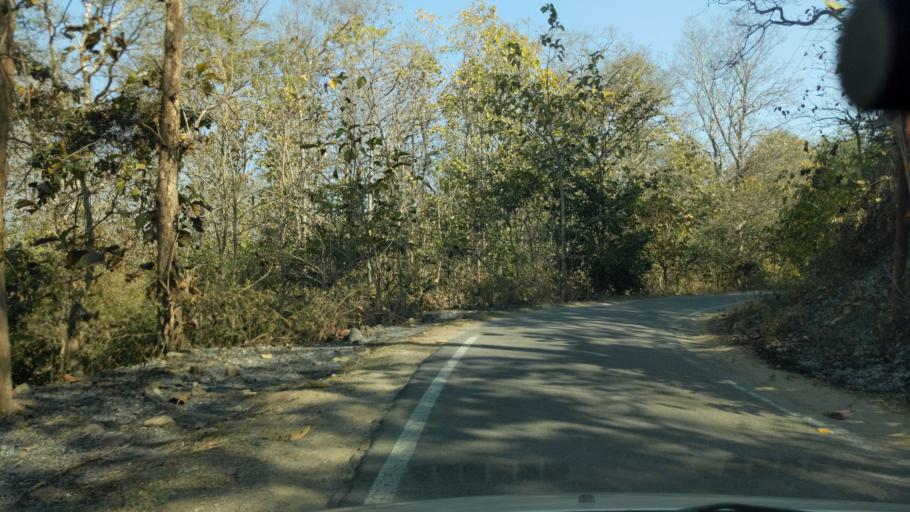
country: IN
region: Uttarakhand
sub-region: Naini Tal
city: Ramnagar
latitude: 29.4018
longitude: 79.1359
